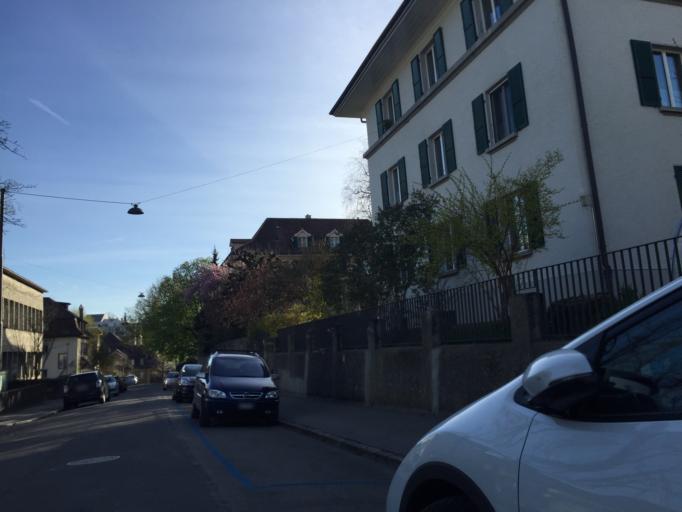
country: CH
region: Bern
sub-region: Bern-Mittelland District
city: Bern
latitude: 46.9526
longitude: 7.4276
